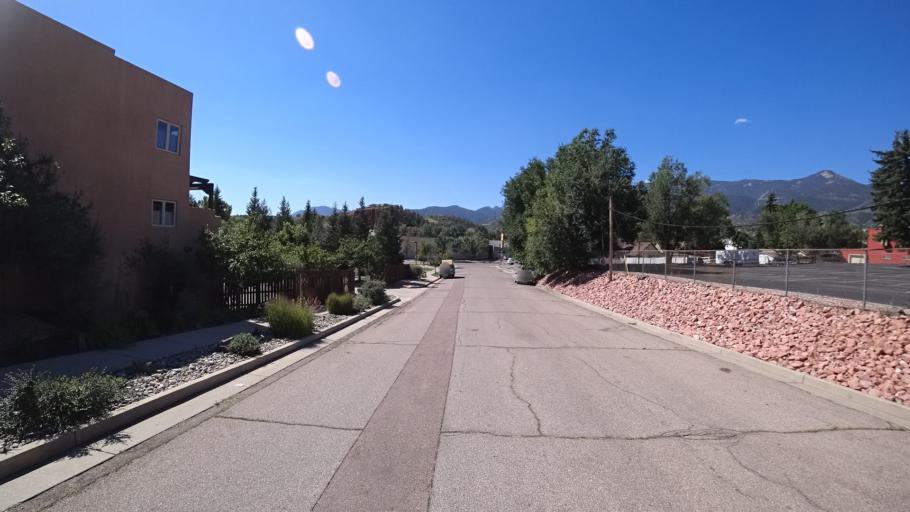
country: US
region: Colorado
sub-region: El Paso County
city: Manitou Springs
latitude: 38.8565
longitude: -104.8764
